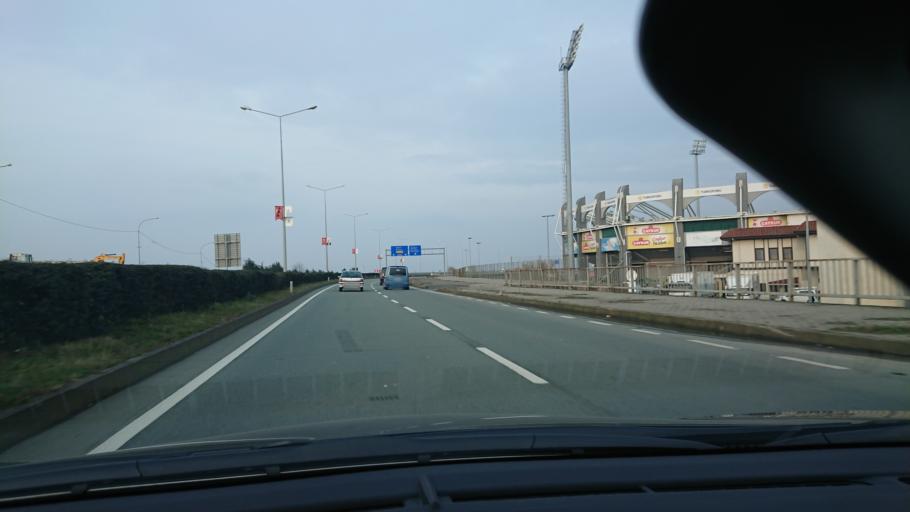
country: TR
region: Rize
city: Gundogdu
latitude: 41.0418
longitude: 40.5715
